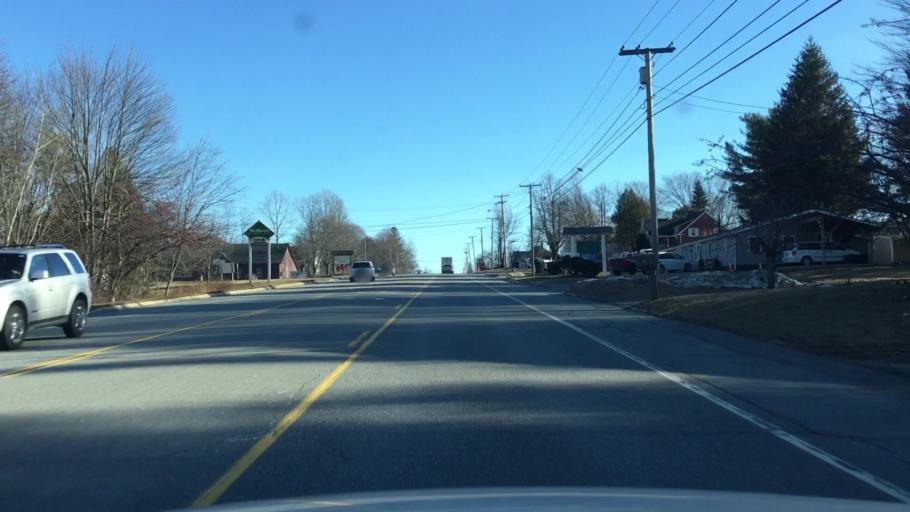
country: US
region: Maine
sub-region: Penobscot County
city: Holden
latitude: 44.7662
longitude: -68.7095
